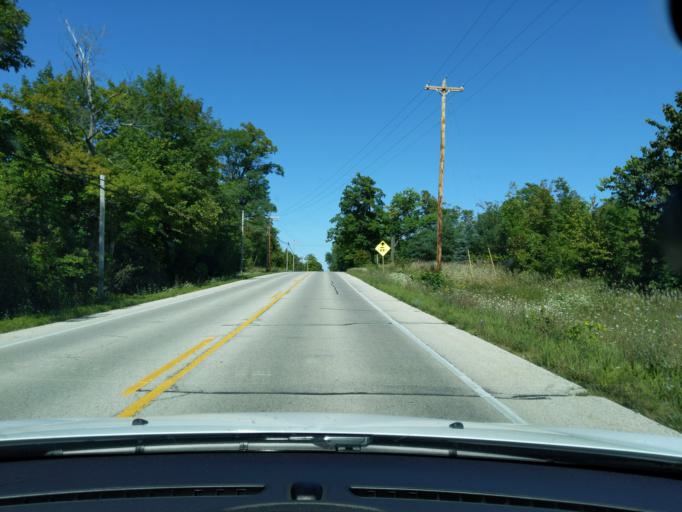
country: US
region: Wisconsin
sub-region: Door County
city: Sturgeon Bay
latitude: 45.2212
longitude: -87.1068
